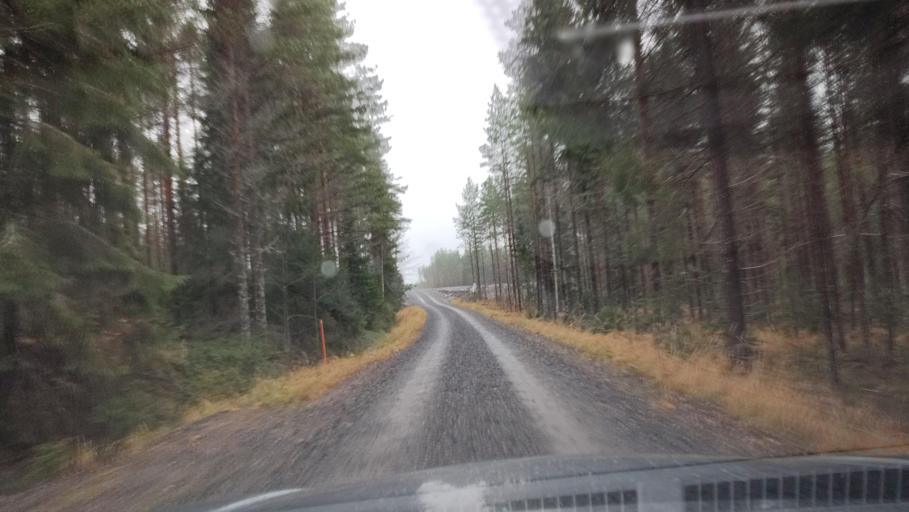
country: FI
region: Southern Ostrobothnia
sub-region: Suupohja
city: Karijoki
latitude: 62.1430
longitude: 21.6271
